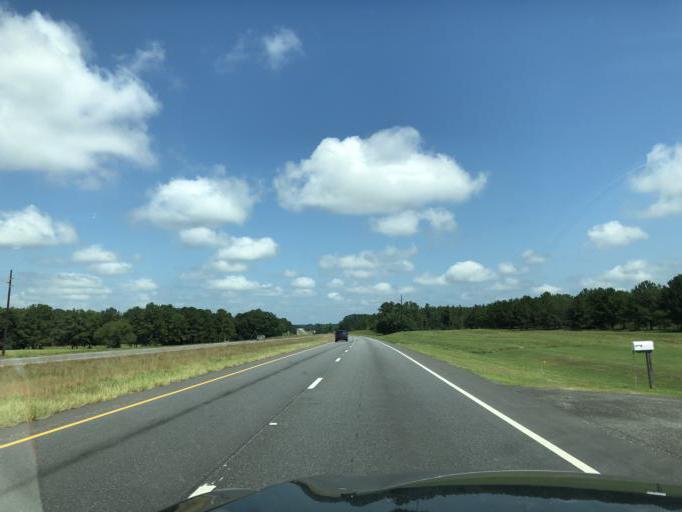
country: US
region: Alabama
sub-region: Henry County
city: Abbeville
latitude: 31.5074
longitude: -85.2912
